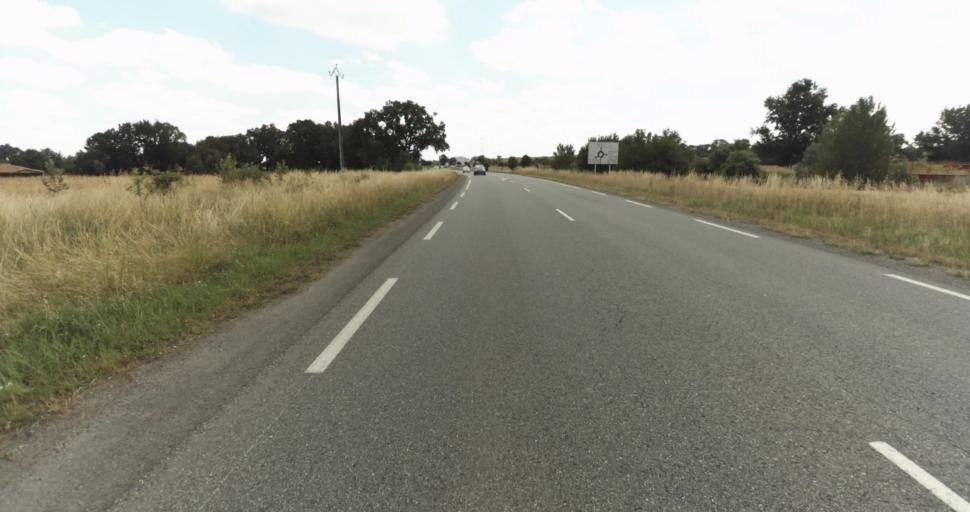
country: FR
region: Midi-Pyrenees
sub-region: Departement de la Haute-Garonne
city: Fontenilles
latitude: 43.5592
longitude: 1.1812
